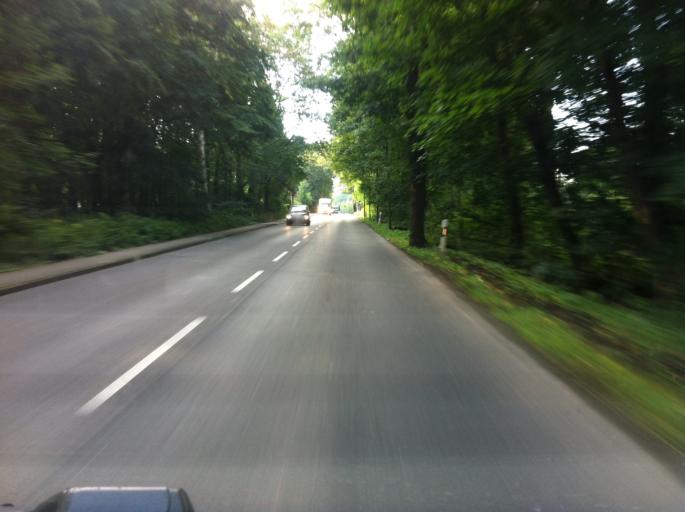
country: DE
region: North Rhine-Westphalia
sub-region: Regierungsbezirk Koln
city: Mengenich
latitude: 50.9725
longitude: 6.8637
